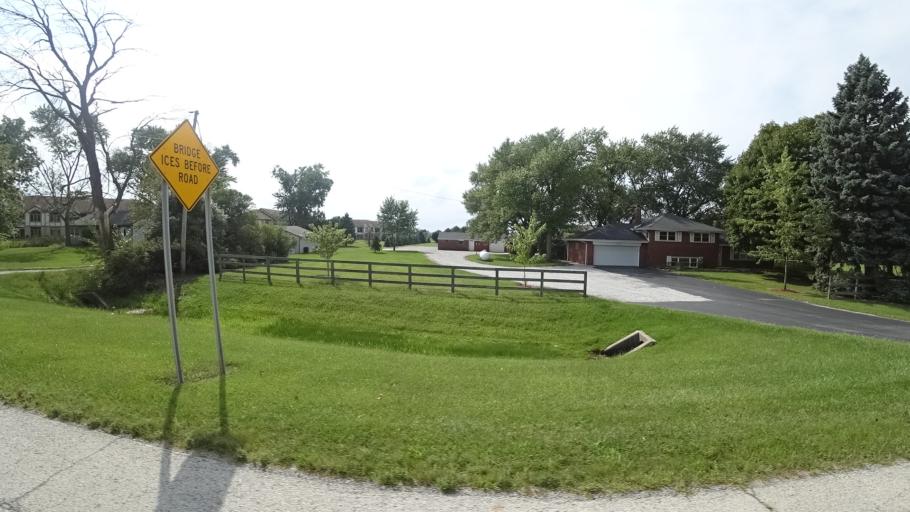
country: US
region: Illinois
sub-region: Cook County
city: Tinley Park
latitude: 41.5555
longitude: -87.7713
